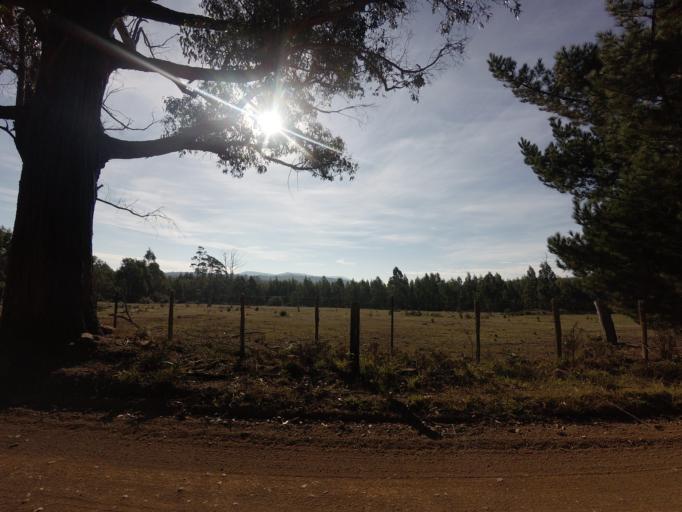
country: AU
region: Tasmania
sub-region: Sorell
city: Sorell
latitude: -42.5049
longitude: 147.5526
